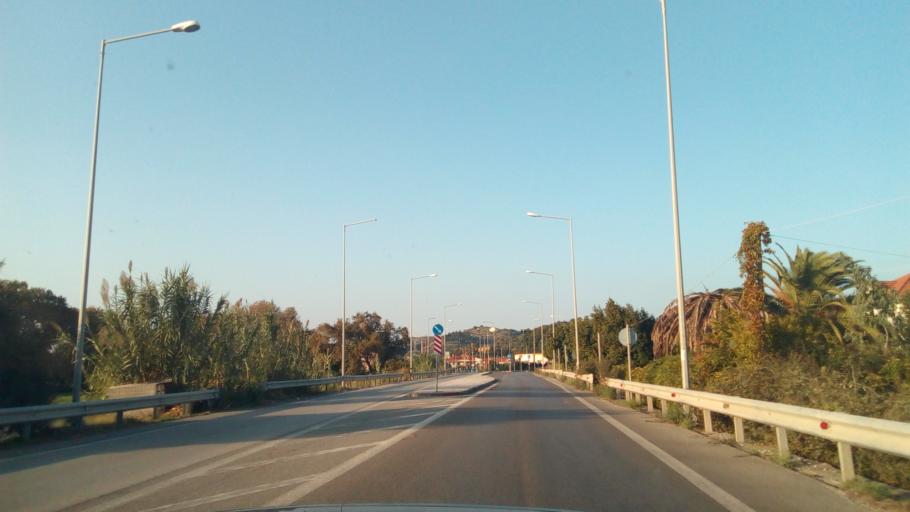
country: GR
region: West Greece
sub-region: Nomos Aitolias kai Akarnanias
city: Antirrio
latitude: 38.3714
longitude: 21.7828
